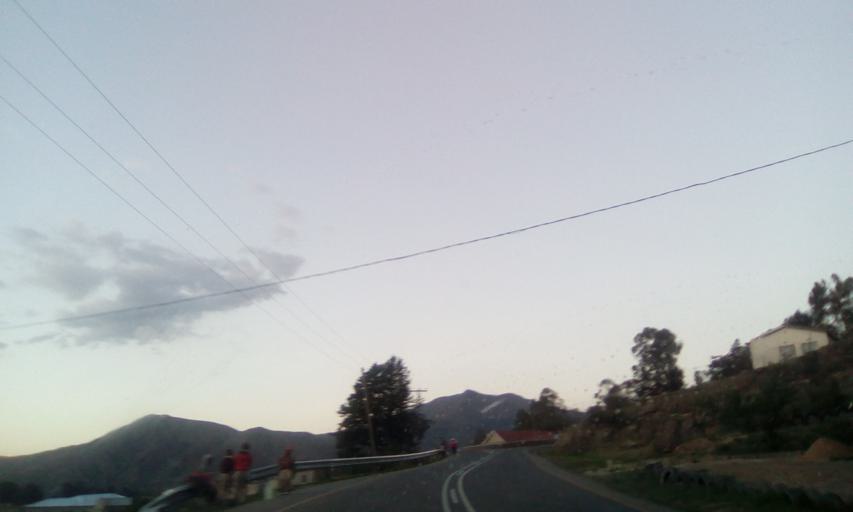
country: LS
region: Qacha's Nek
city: Qacha's Nek
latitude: -30.1209
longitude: 28.6860
